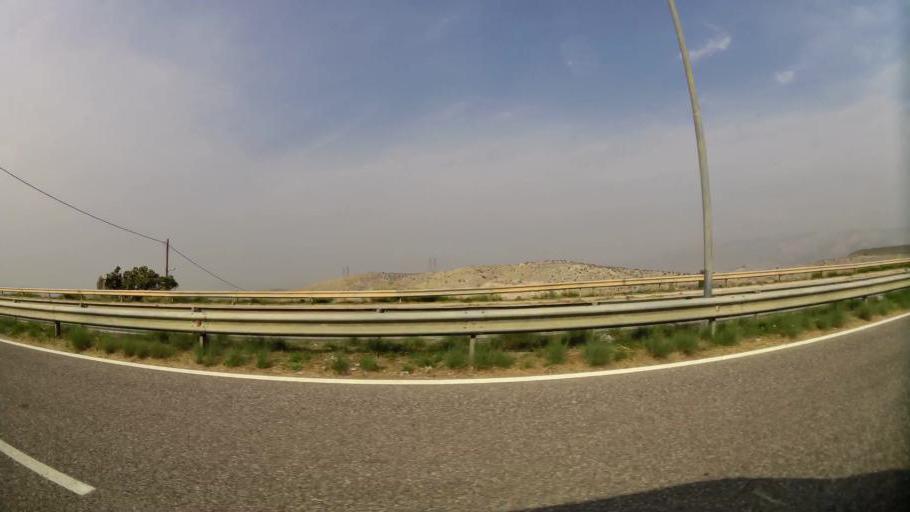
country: GR
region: Attica
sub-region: Nomarchia Athinas
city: Chaidari
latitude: 38.0443
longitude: 23.6439
